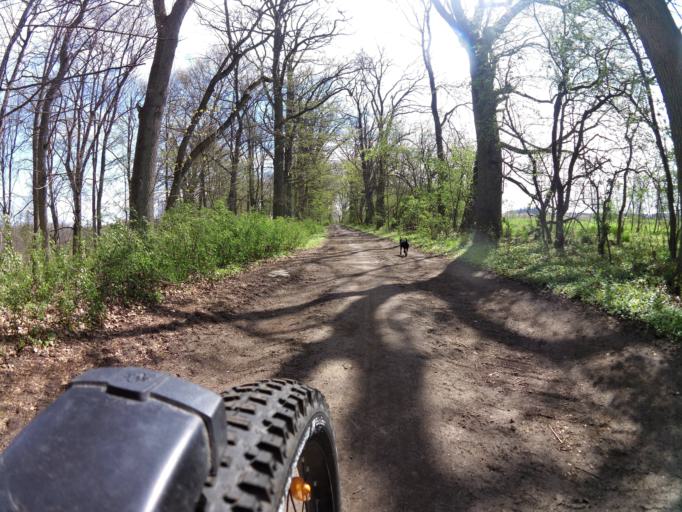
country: PL
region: West Pomeranian Voivodeship
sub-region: Powiat gryficki
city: Ploty
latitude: 53.7488
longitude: 15.3230
